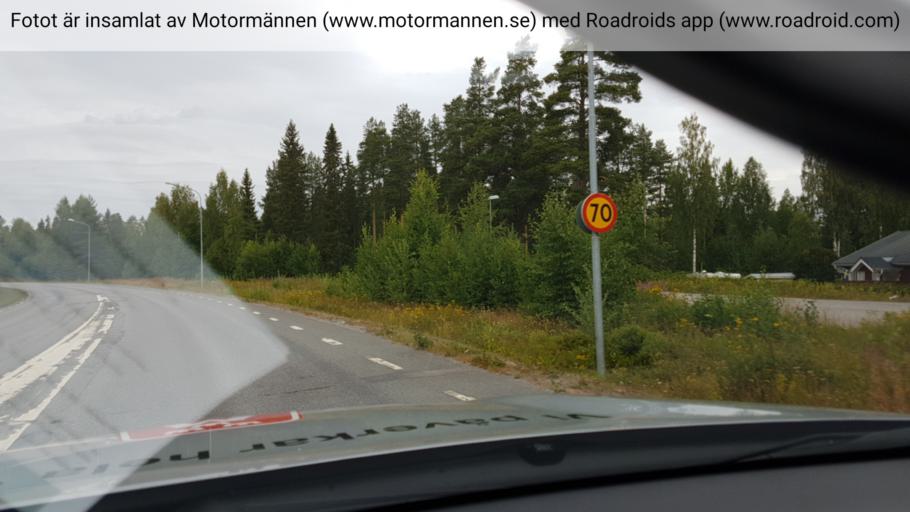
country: SE
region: Norrbotten
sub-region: Bodens Kommun
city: Boden
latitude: 65.8157
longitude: 21.6457
